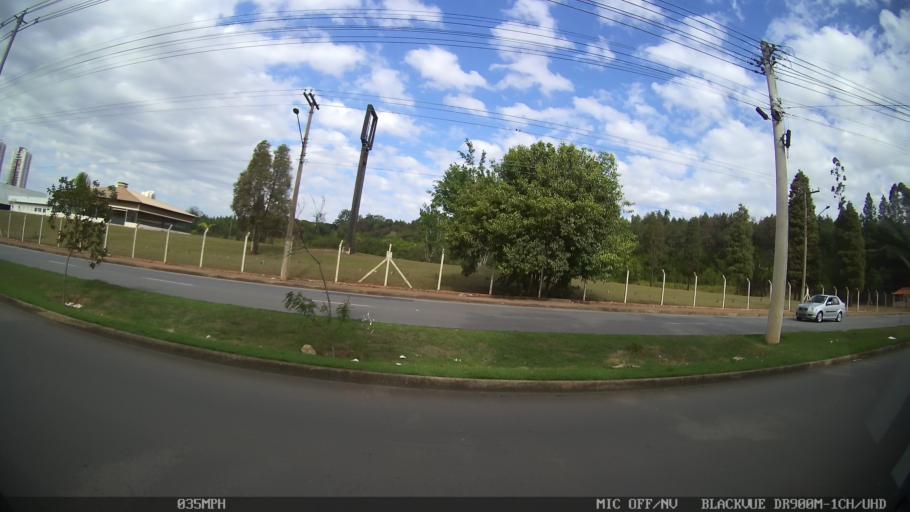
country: BR
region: Sao Paulo
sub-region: Limeira
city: Limeira
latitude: -22.5466
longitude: -47.4239
